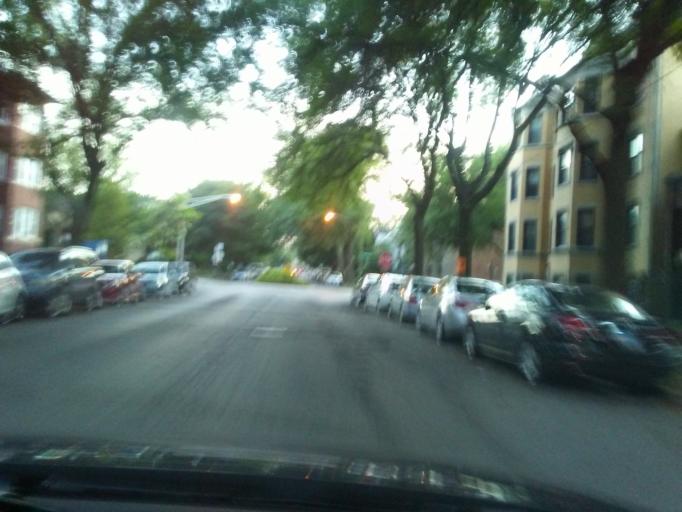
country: US
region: Illinois
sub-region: Cook County
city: Evanston
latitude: 42.0031
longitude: -87.6705
